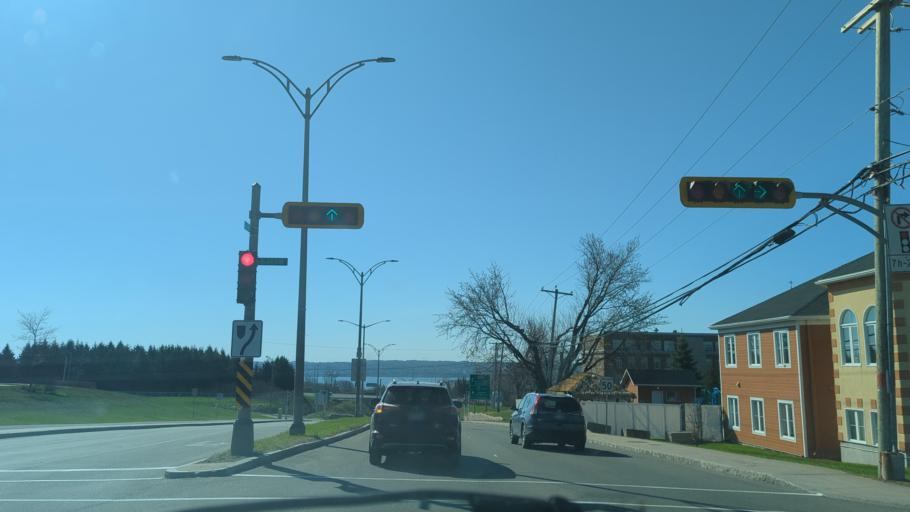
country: CA
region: Quebec
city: Quebec
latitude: 46.8586
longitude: -71.2205
